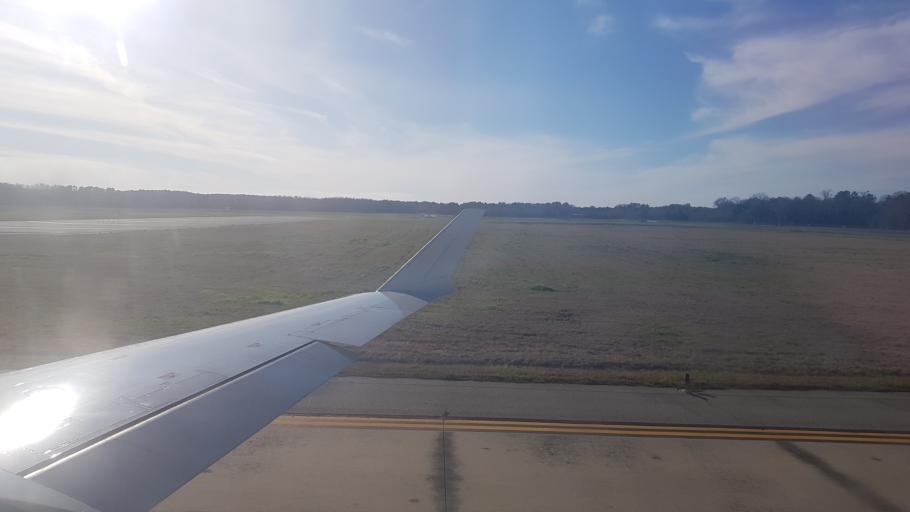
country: US
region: Georgia
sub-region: Chatham County
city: Pooler
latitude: 32.1296
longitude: -81.2187
